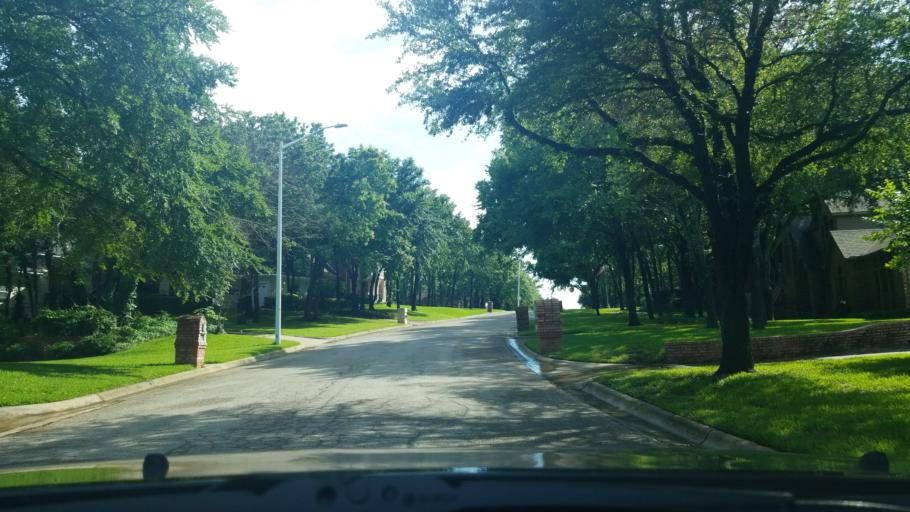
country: US
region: Texas
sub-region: Denton County
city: Denton
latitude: 33.1832
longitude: -97.1105
